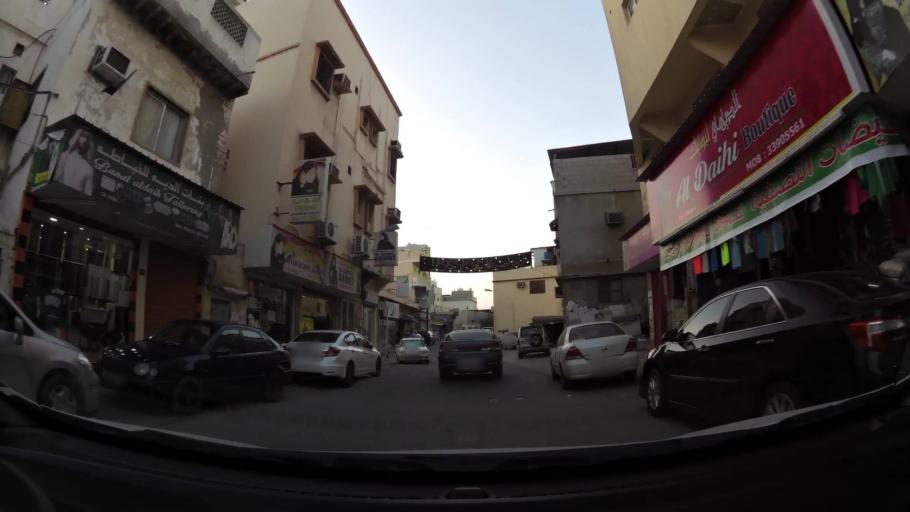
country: BH
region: Manama
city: Jidd Hafs
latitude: 26.2236
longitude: 50.5351
